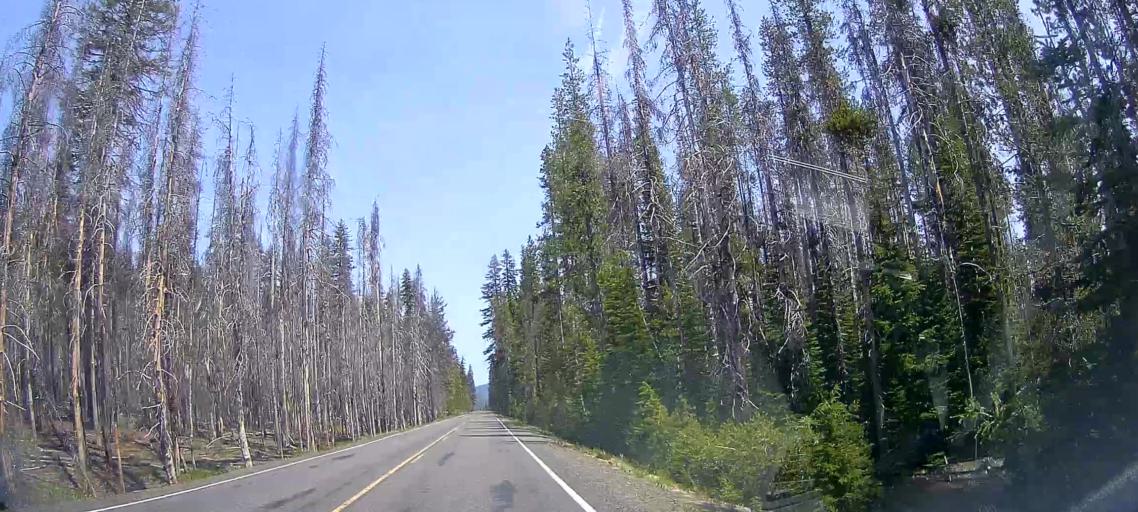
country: US
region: Oregon
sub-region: Lane County
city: Oakridge
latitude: 43.0623
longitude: -122.1208
